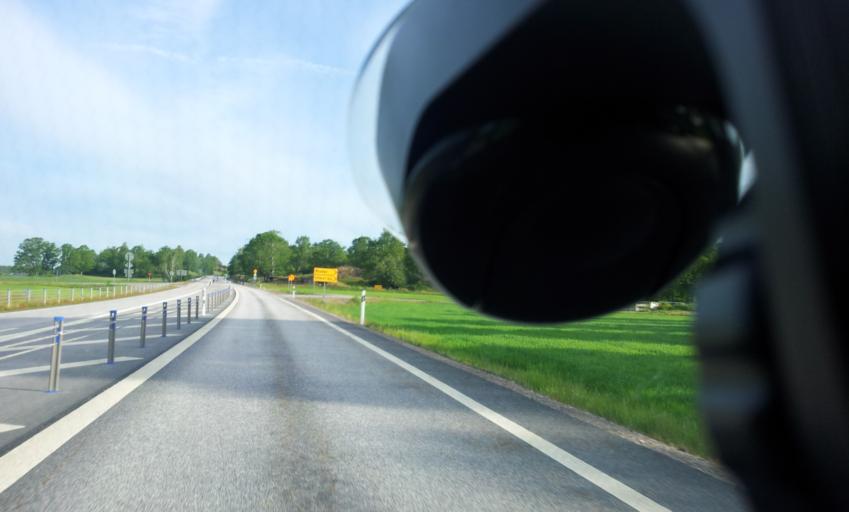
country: SE
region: Kalmar
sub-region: Vasterviks Kommun
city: Gamleby
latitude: 57.8780
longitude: 16.3994
